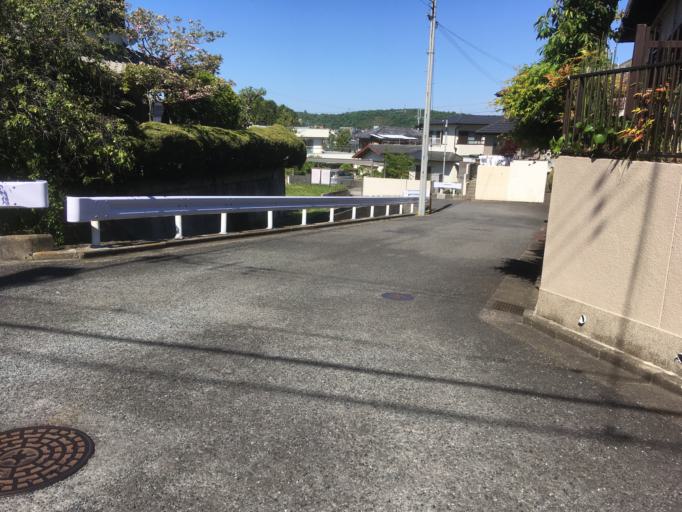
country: JP
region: Nara
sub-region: Ikoma-shi
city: Ikoma
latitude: 34.6852
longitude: 135.6979
